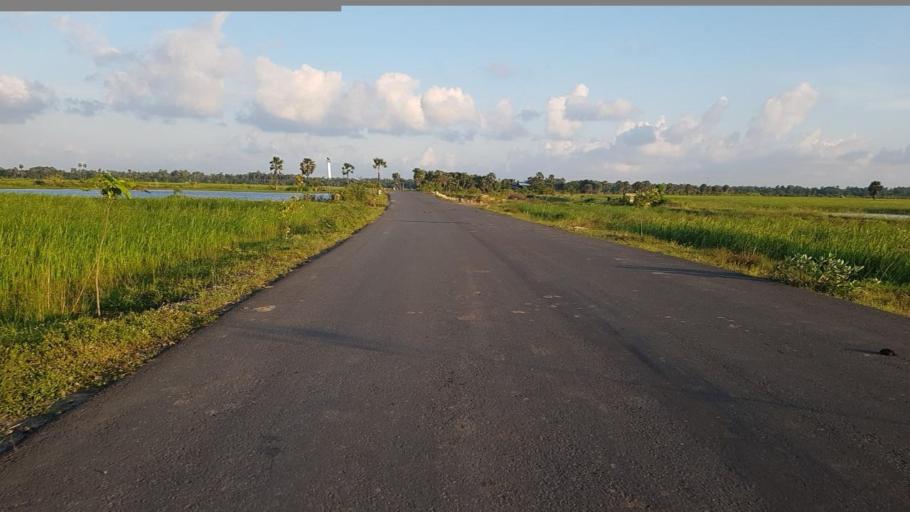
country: LK
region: Northern Province
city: Jaffna
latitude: 9.7283
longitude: 79.9710
